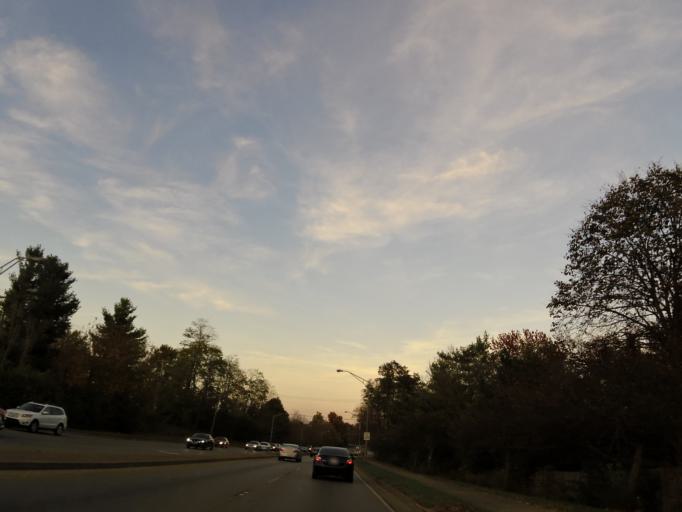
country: US
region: Kentucky
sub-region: Fayette County
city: Lexington
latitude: 37.9910
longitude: -84.4560
